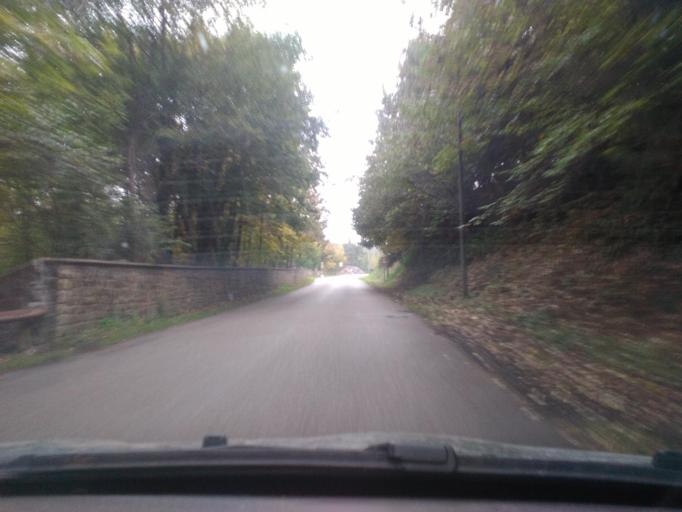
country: FR
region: Lorraine
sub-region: Departement des Vosges
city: Senones
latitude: 48.3968
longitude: 6.9867
